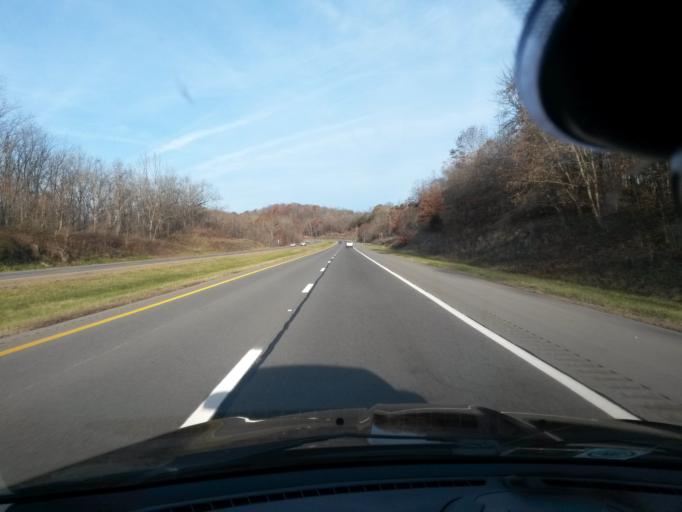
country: US
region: West Virginia
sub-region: Greenbrier County
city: Lewisburg
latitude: 37.8543
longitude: -80.5085
